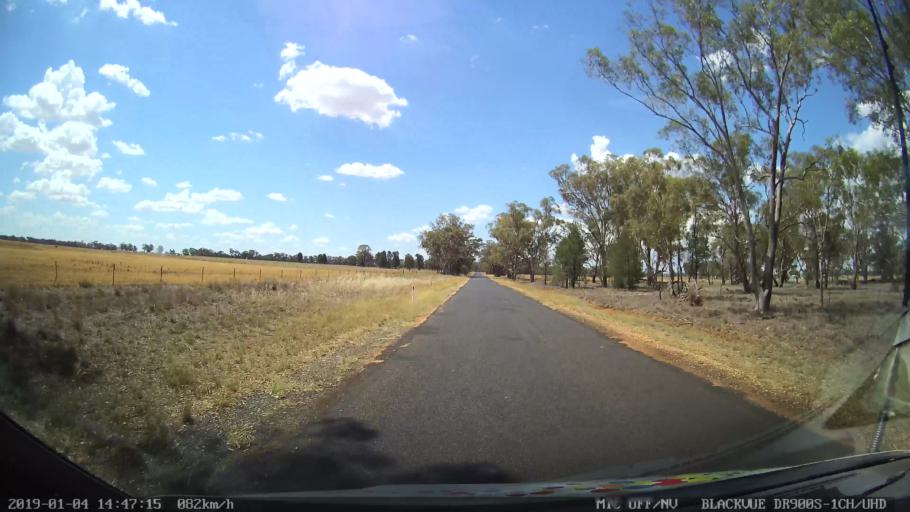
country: AU
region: New South Wales
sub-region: Dubbo Municipality
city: Dubbo
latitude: -32.0714
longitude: 148.6598
